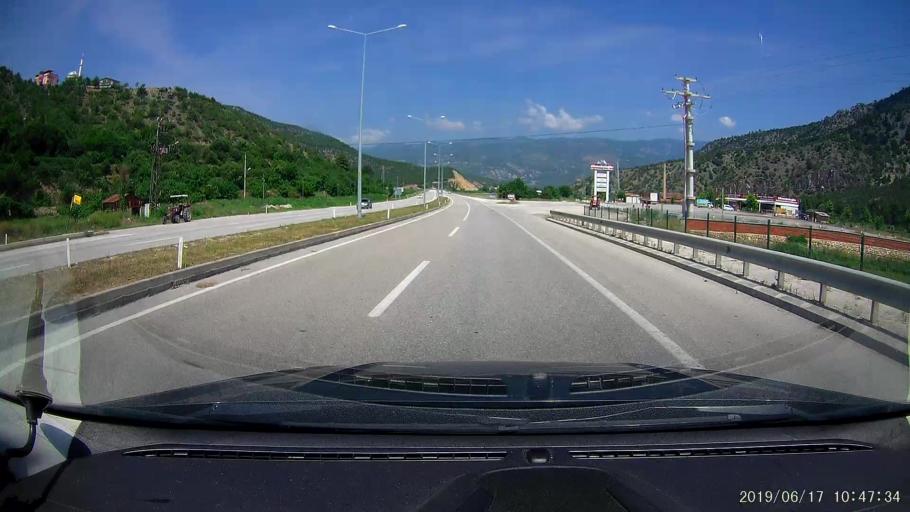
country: TR
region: Corum
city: Hacihamza
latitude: 41.0784
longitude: 34.4470
